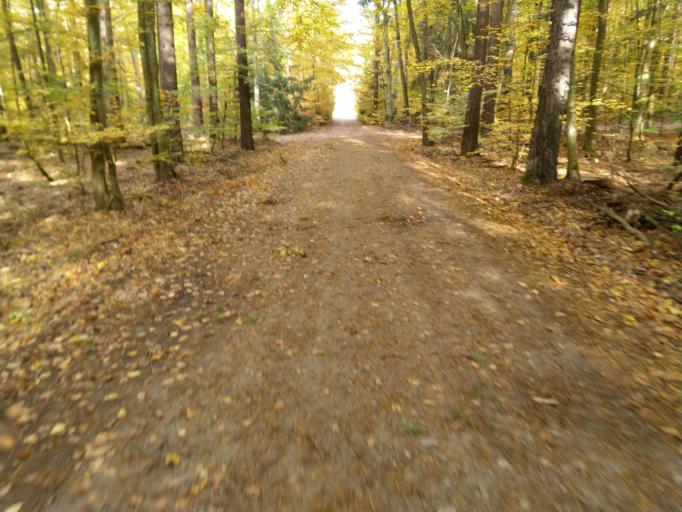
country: DE
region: Brandenburg
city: Melchow
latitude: 52.7984
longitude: 13.7007
